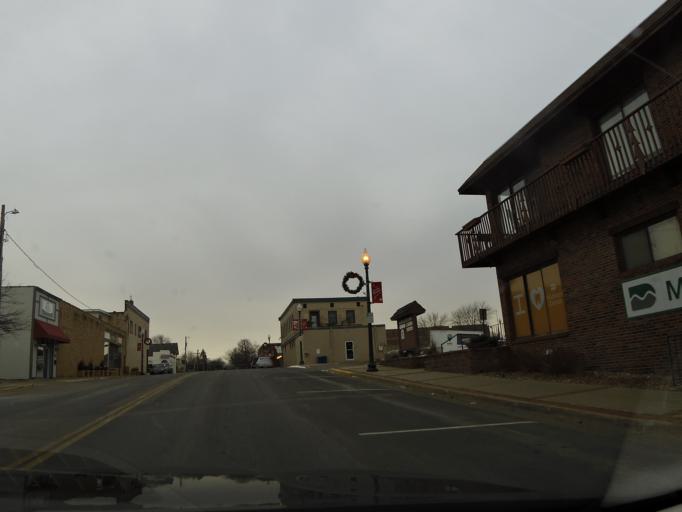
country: US
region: Minnesota
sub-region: Carver County
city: Waconia
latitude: 44.8502
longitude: -93.7876
